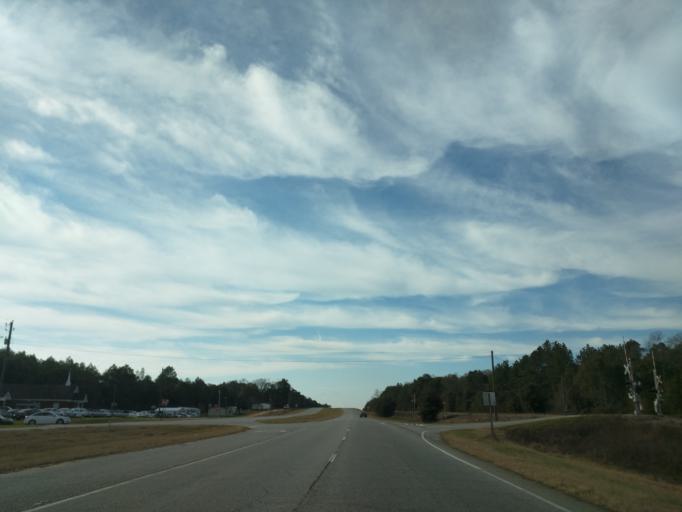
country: US
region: Georgia
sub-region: Decatur County
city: Bainbridge
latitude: 30.8983
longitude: -84.5145
